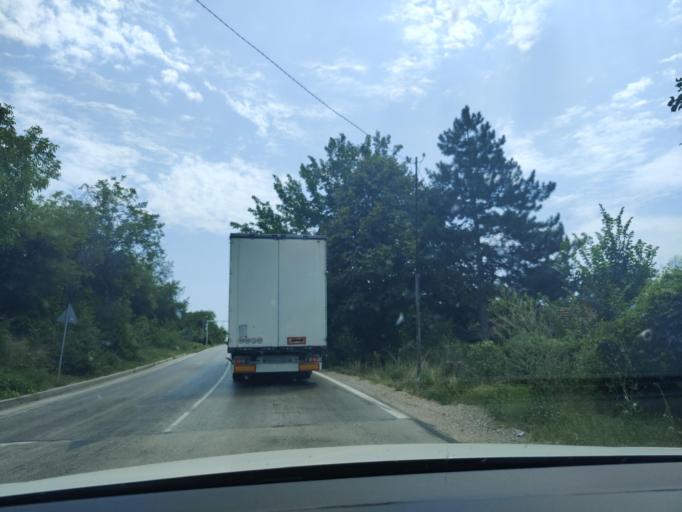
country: BG
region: Vidin
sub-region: Obshtina Ruzhintsi
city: Ruzhintsi
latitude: 43.6515
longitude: 22.7899
